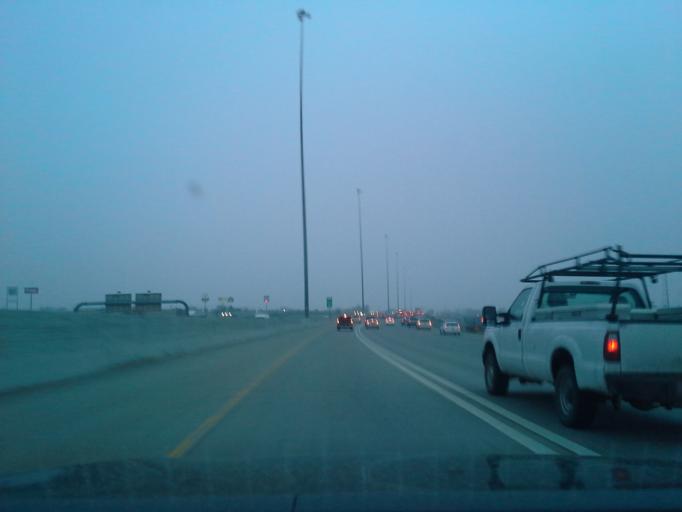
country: US
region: Utah
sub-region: Salt Lake County
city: Midvale
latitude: 40.6249
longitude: -111.9030
